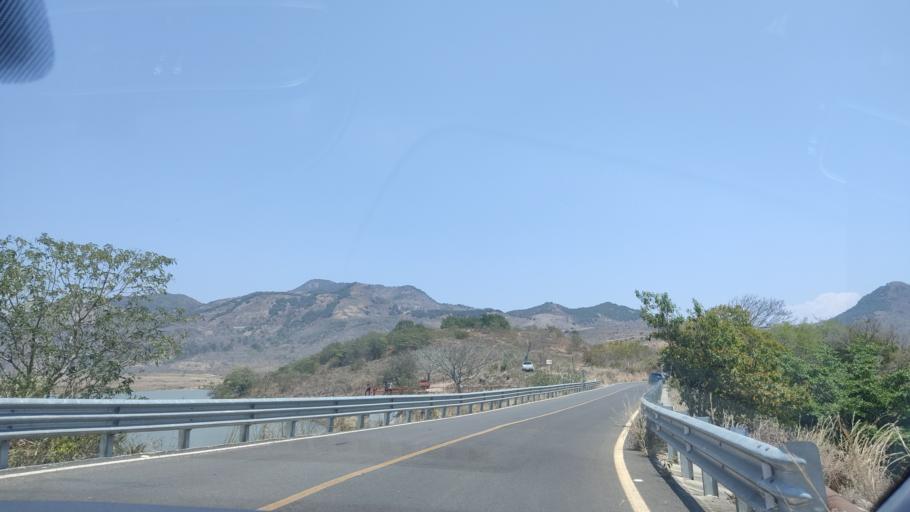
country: MX
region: Nayarit
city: Puga
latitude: 21.6067
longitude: -104.7396
